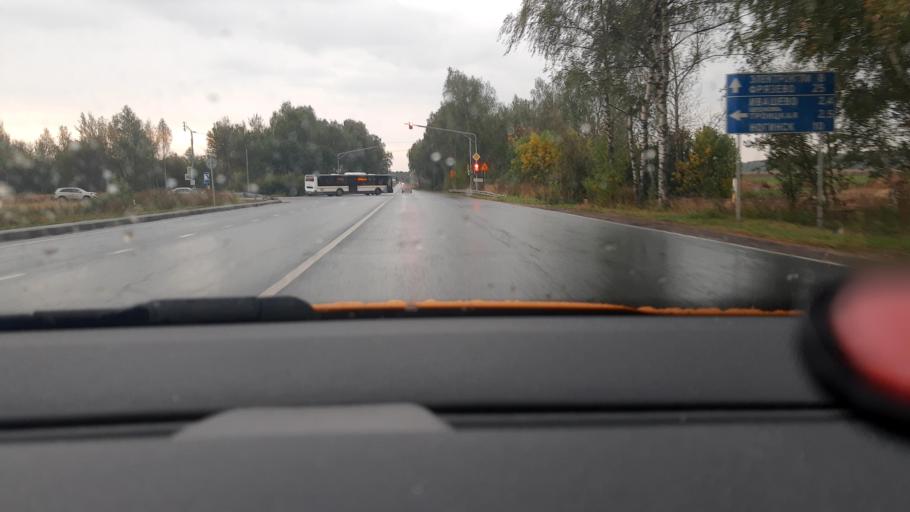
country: RU
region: Moskovskaya
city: Obukhovo
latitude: 55.8001
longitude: 38.2507
